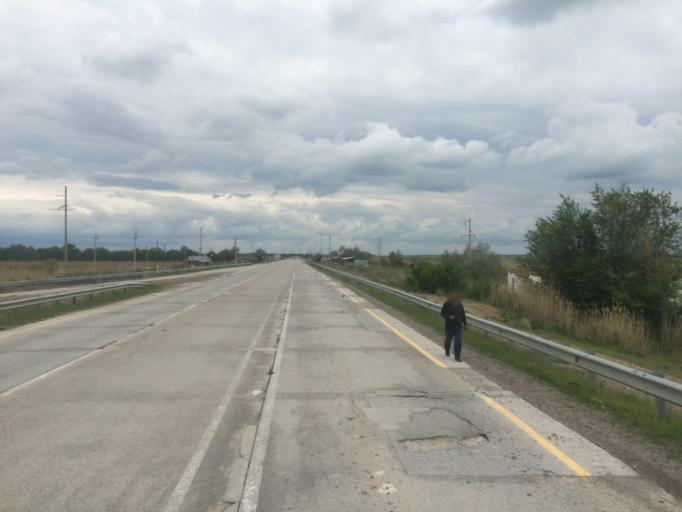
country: KG
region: Chuy
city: Sokuluk
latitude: 43.2726
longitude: 74.2367
